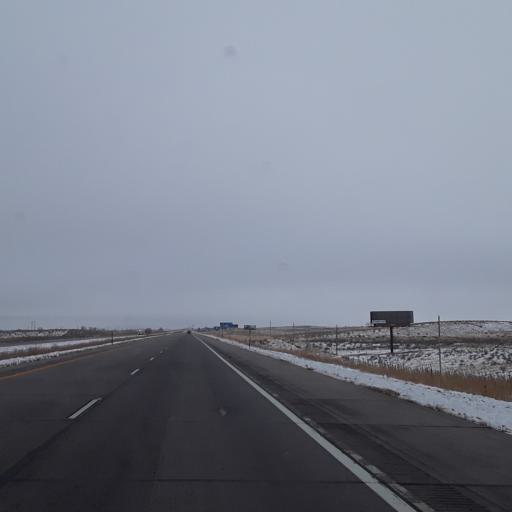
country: US
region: Colorado
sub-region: Logan County
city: Sterling
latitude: 40.5942
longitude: -103.1887
